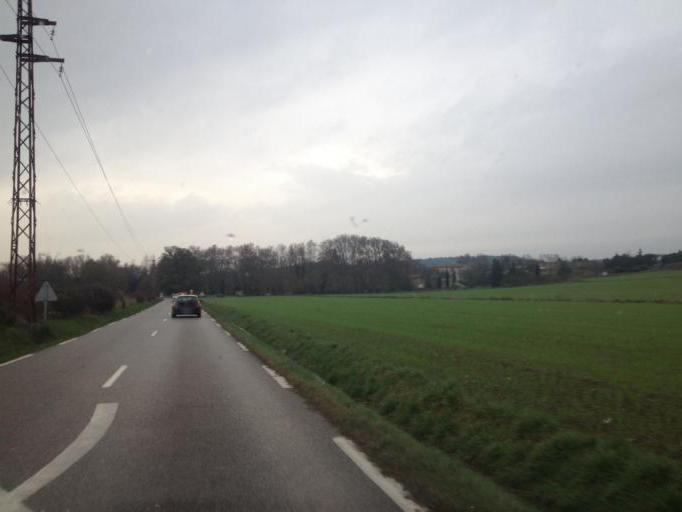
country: FR
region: Provence-Alpes-Cote d'Azur
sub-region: Departement des Bouches-du-Rhone
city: Eguilles
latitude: 43.5098
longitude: 5.3500
